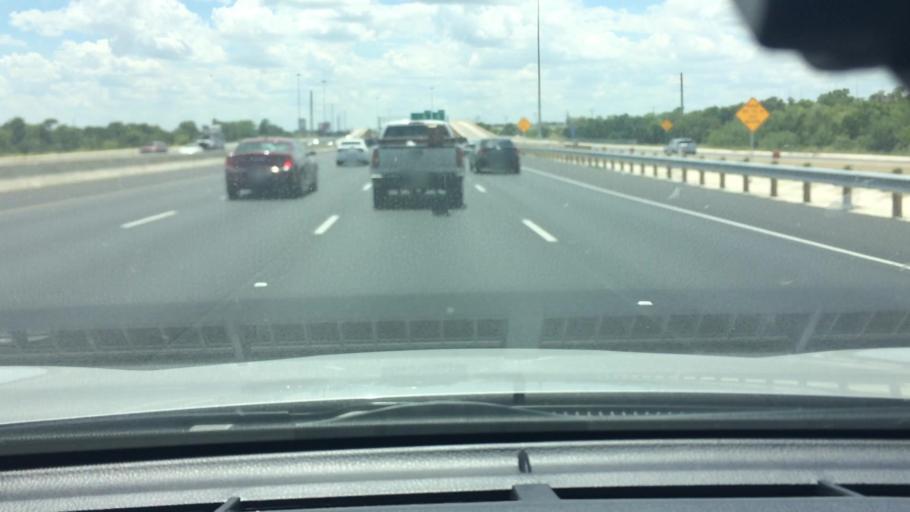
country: US
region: Texas
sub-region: Bexar County
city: Leon Valley
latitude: 29.4516
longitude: -98.6315
